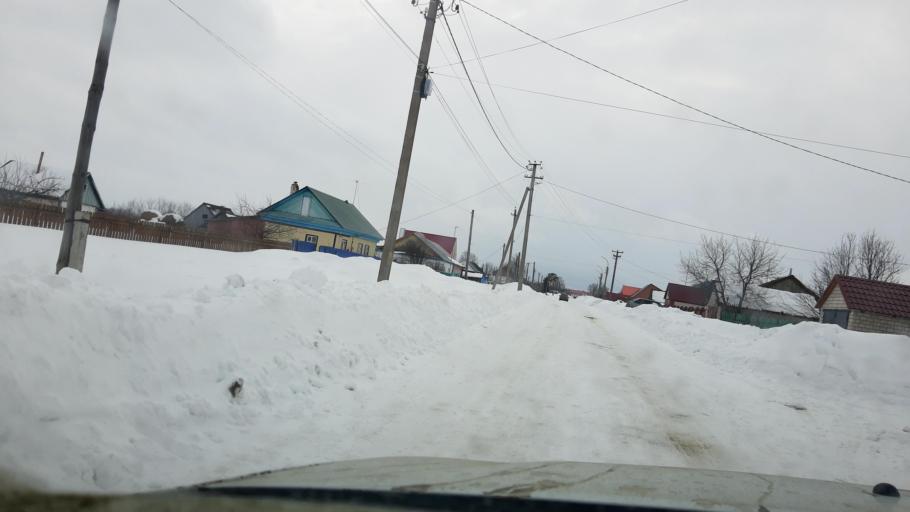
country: RU
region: Bashkortostan
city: Karmaskaly
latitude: 54.4183
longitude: 56.1653
